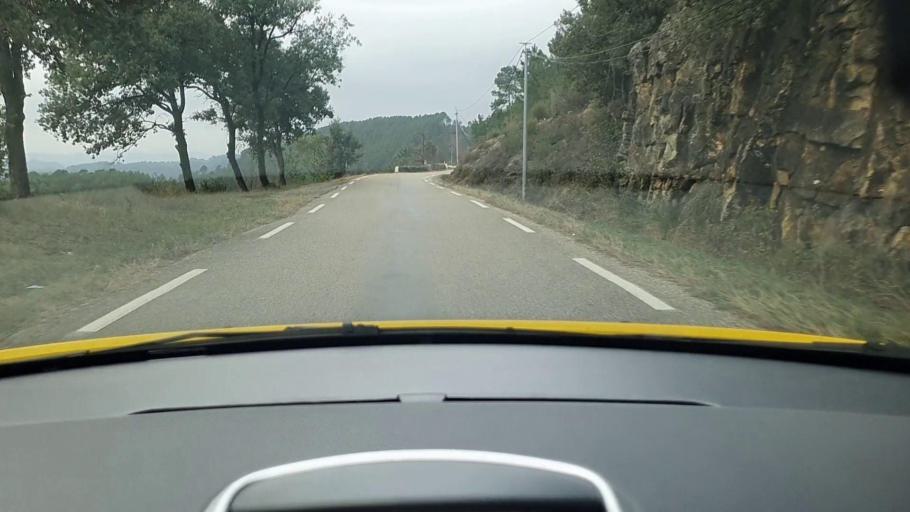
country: FR
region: Languedoc-Roussillon
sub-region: Departement du Gard
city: Besseges
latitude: 44.3095
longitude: 4.0785
